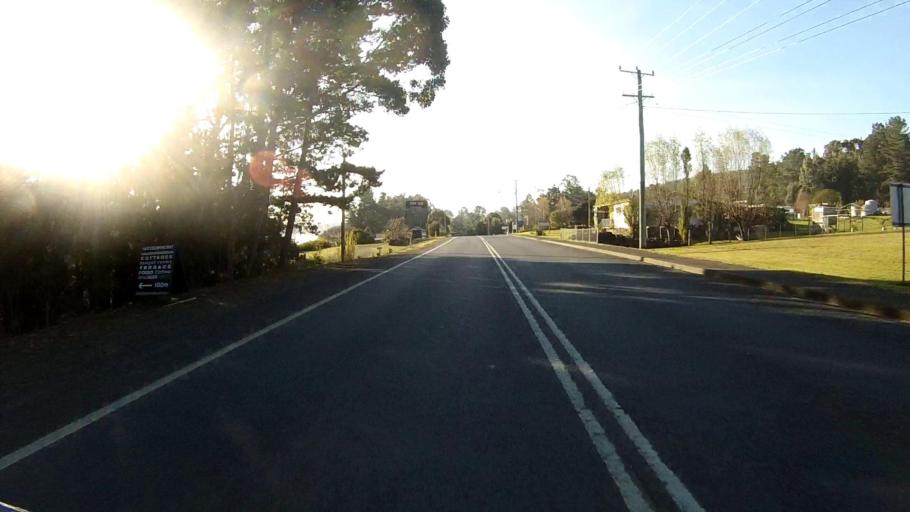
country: AU
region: Tasmania
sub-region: Clarence
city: Sandford
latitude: -43.0567
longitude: 147.8651
